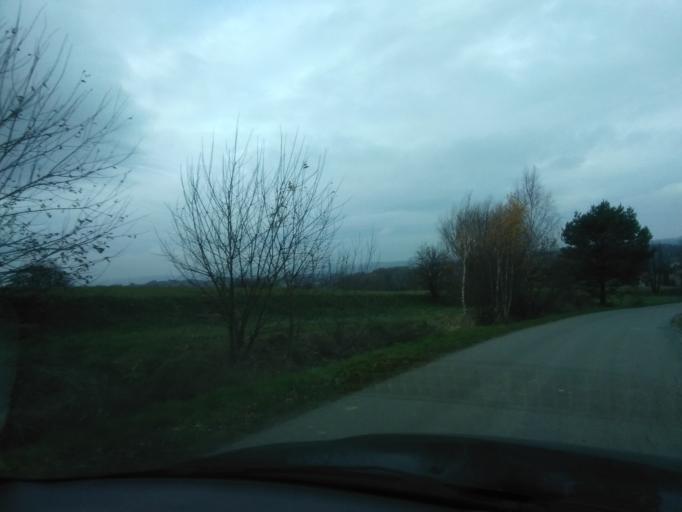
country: PL
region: Subcarpathian Voivodeship
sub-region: Powiat strzyzowski
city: Wysoka Strzyzowska
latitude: 49.8387
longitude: 21.7752
